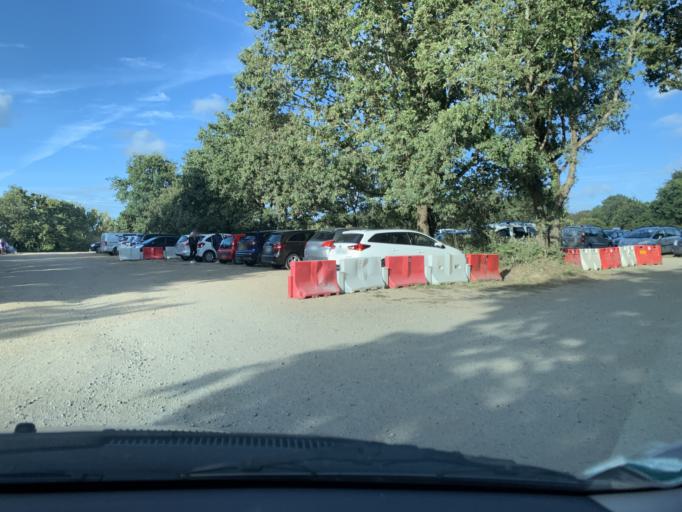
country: FR
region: Brittany
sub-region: Departement du Morbihan
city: Sarzeau
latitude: 47.5155
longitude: -2.7267
